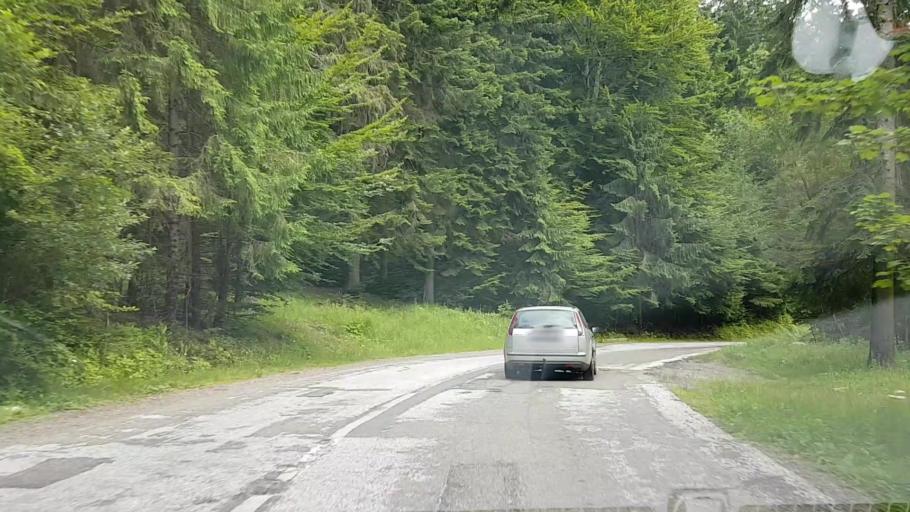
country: RO
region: Neamt
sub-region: Comuna Pangarati
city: Pangarati
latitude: 46.9707
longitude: 26.1176
